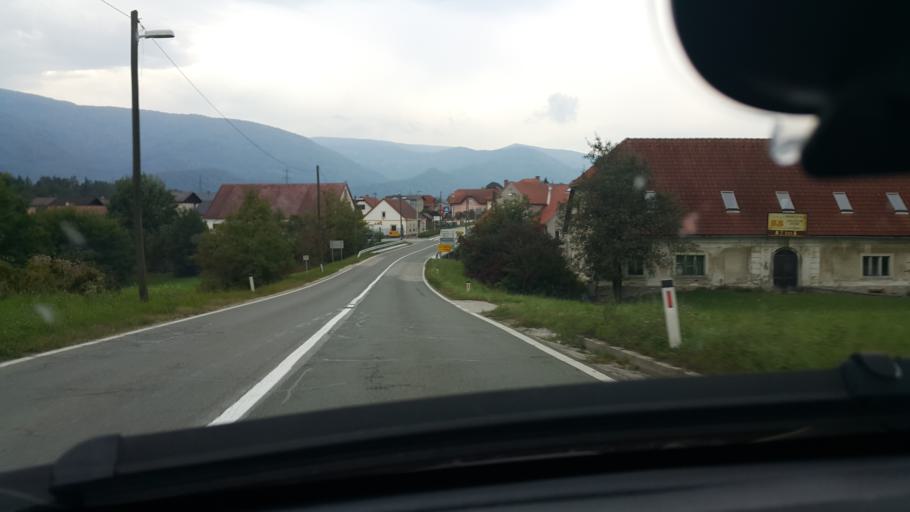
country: SI
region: Ruse
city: Ruse
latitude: 46.5568
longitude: 15.5155
